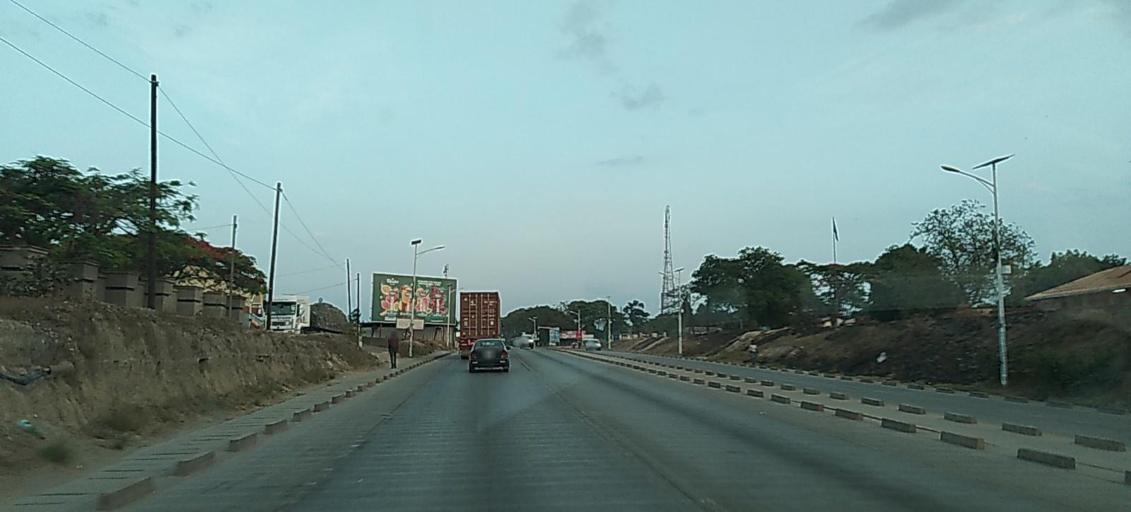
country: ZM
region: Copperbelt
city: Chingola
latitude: -12.5469
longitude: 27.8550
